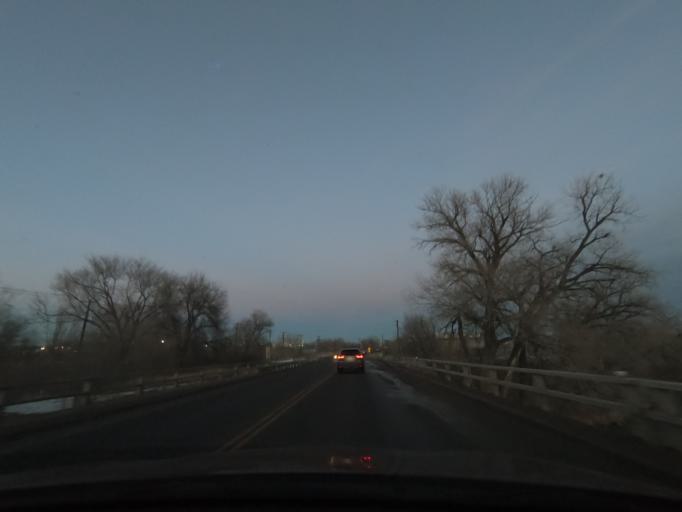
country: US
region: Colorado
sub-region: El Paso County
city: Stratmoor
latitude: 38.7767
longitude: -104.7789
